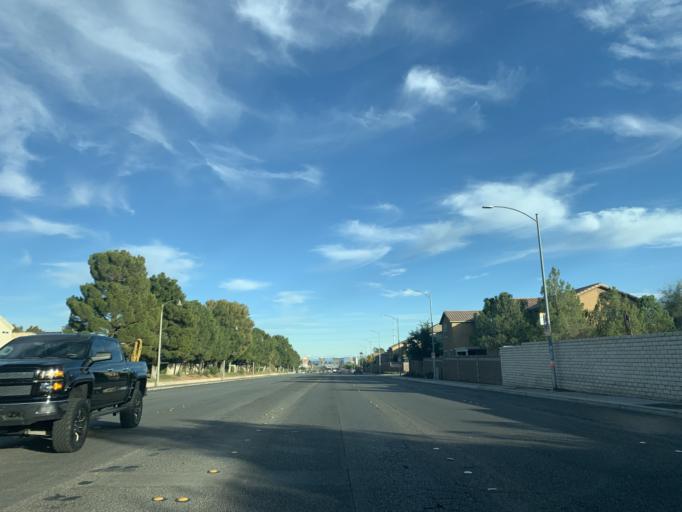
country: US
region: Nevada
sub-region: Clark County
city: Spring Valley
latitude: 36.1296
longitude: -115.2827
